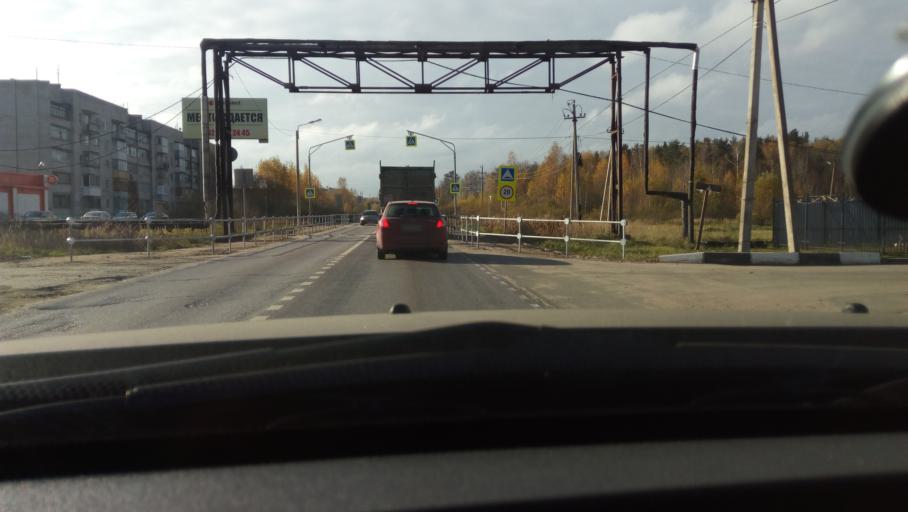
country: RU
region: Moskovskaya
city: Fryazevo
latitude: 55.7126
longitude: 38.4591
